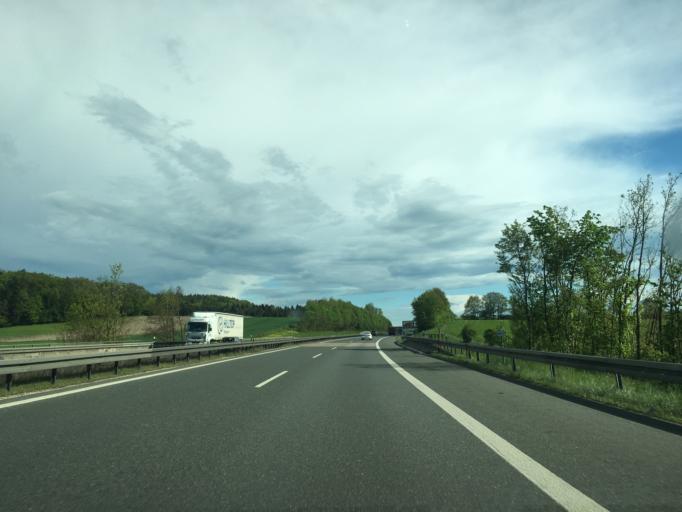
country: DE
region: Bavaria
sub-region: Upper Palatinate
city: Pilsach
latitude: 49.3373
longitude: 11.4526
